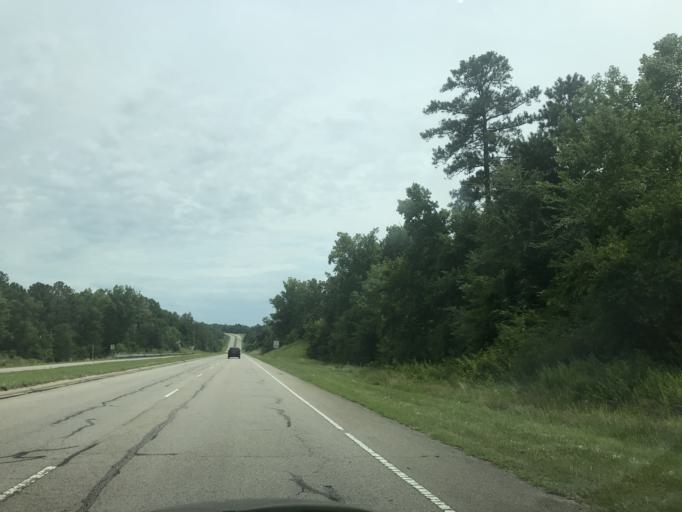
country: US
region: North Carolina
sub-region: Vance County
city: South Henderson
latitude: 36.3207
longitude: -78.4494
